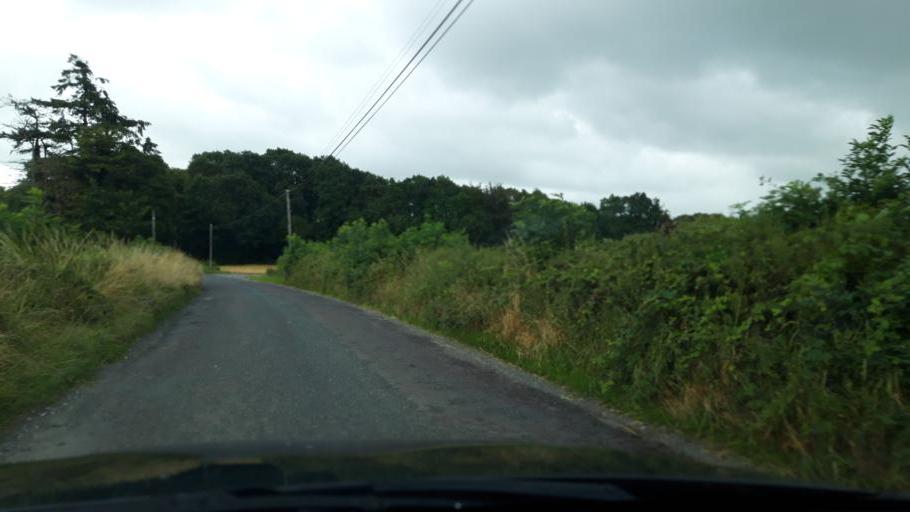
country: IE
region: Munster
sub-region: County Cork
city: Youghal
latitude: 52.1272
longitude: -7.9735
